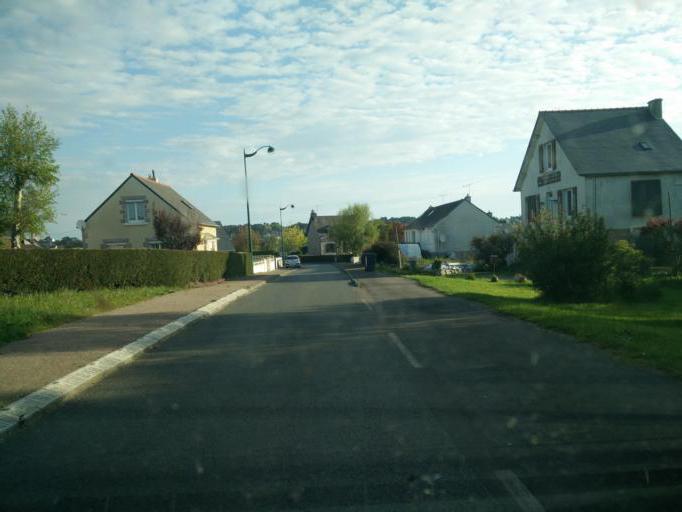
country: FR
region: Brittany
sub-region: Departement des Cotes-d'Armor
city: Erquy
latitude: 48.6276
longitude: -2.4547
